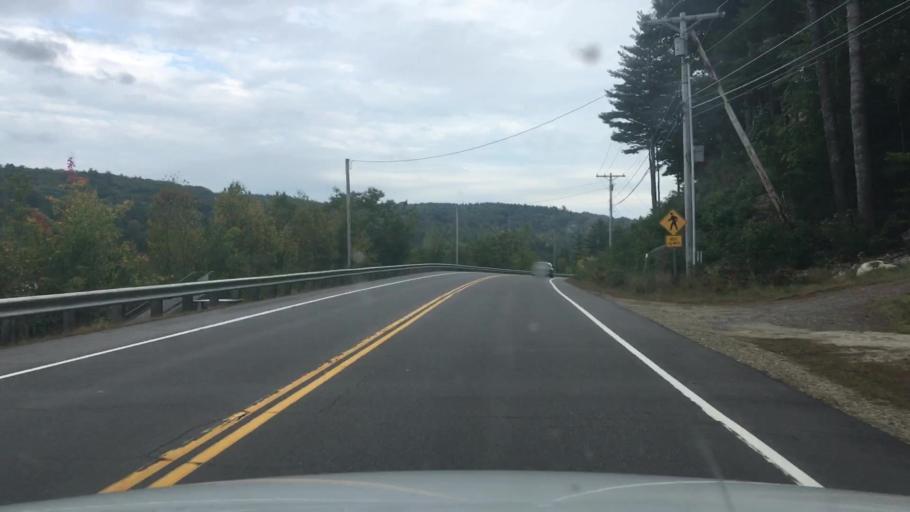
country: US
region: New Hampshire
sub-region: Strafford County
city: New Durham
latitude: 43.4844
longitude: -71.2443
